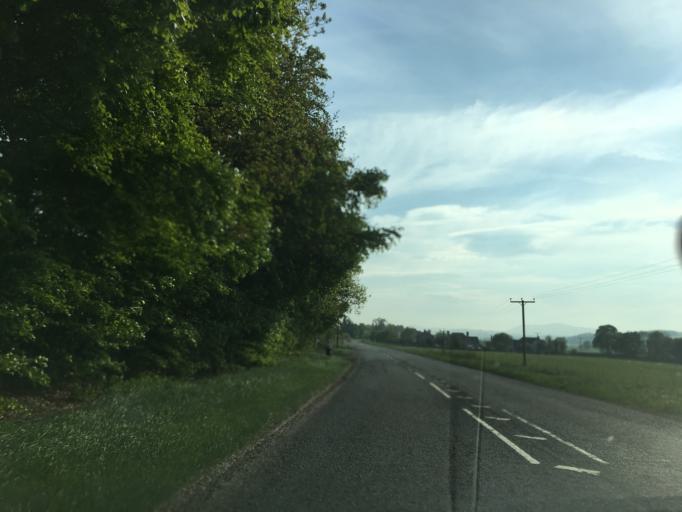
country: GB
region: Scotland
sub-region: The Scottish Borders
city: West Linton
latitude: 55.7500
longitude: -3.2849
